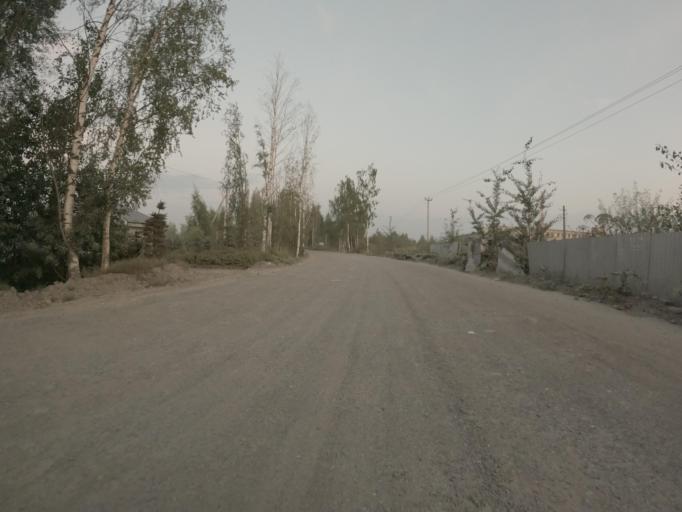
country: RU
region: Leningrad
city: Yanino Vtoroye
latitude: 59.9432
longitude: 30.5978
